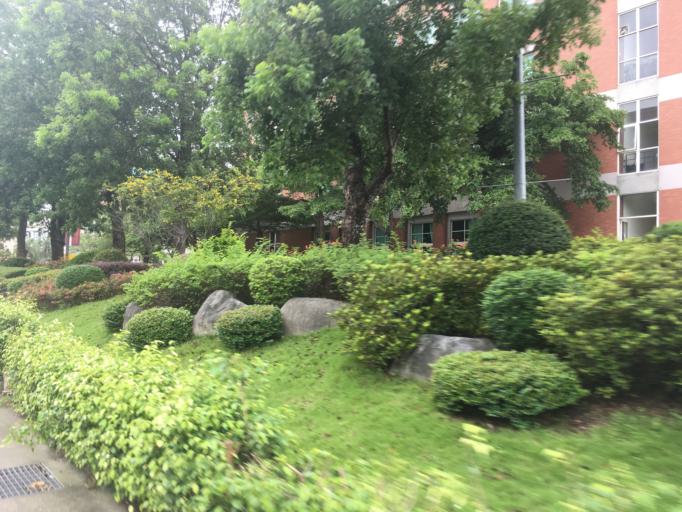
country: TW
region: Taiwan
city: Zhongxing New Village
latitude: 24.0478
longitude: 120.6871
